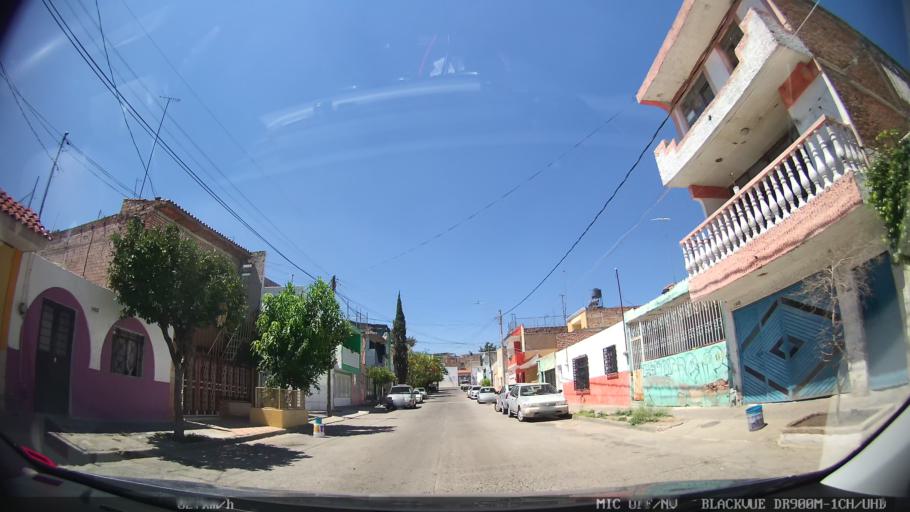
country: MX
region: Jalisco
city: Tlaquepaque
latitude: 20.6930
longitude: -103.2932
